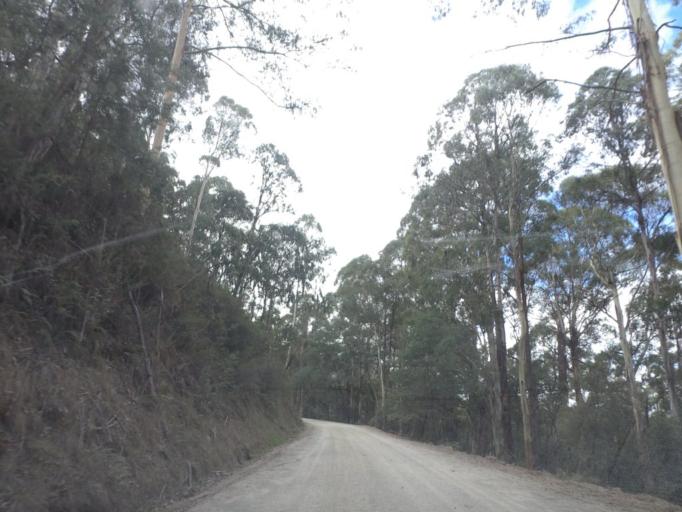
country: AU
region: Victoria
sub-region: Yarra Ranges
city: Millgrove
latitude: -37.5160
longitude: 145.9512
